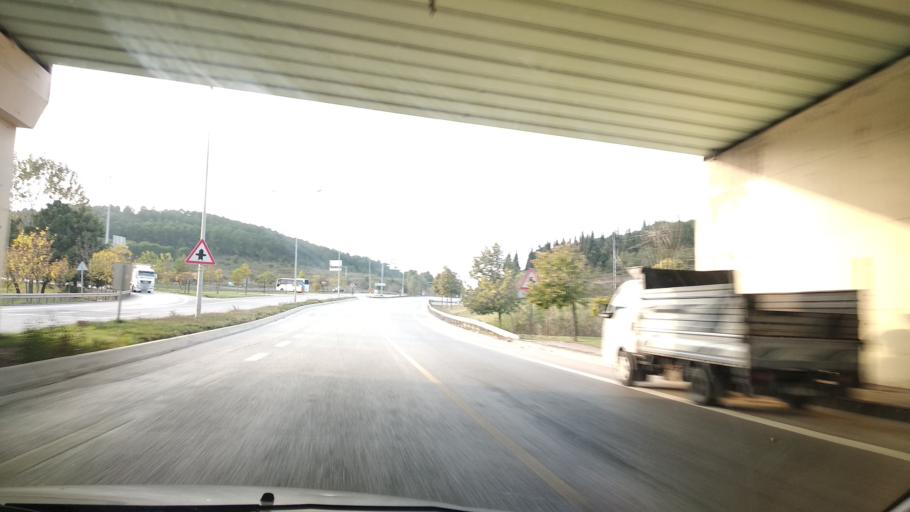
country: TR
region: Istanbul
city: Sultanbeyli
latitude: 40.9225
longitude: 29.3409
